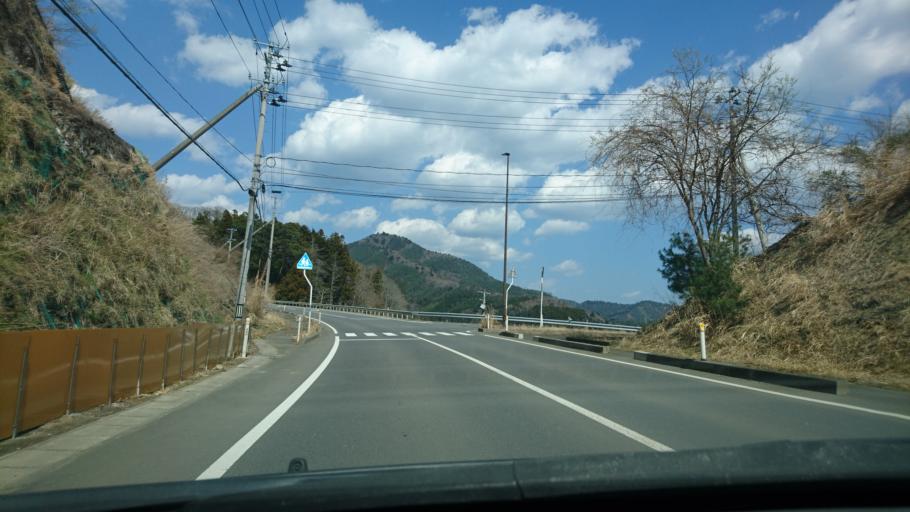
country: JP
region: Miyagi
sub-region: Oshika Gun
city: Onagawa Cho
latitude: 38.5051
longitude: 141.4863
